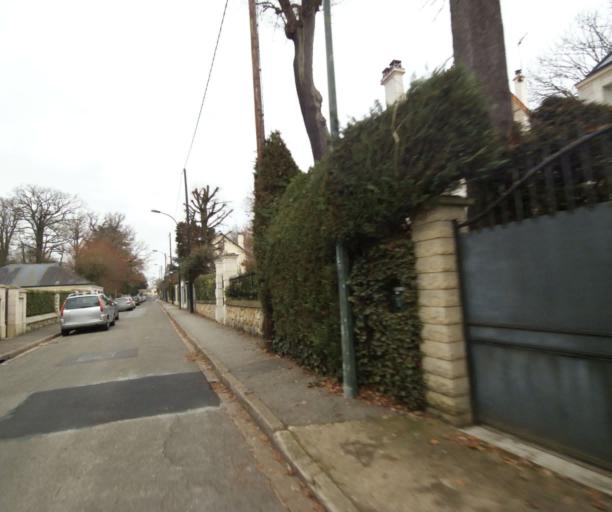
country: FR
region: Ile-de-France
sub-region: Departement des Hauts-de-Seine
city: Garches
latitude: 48.8429
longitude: 2.1741
